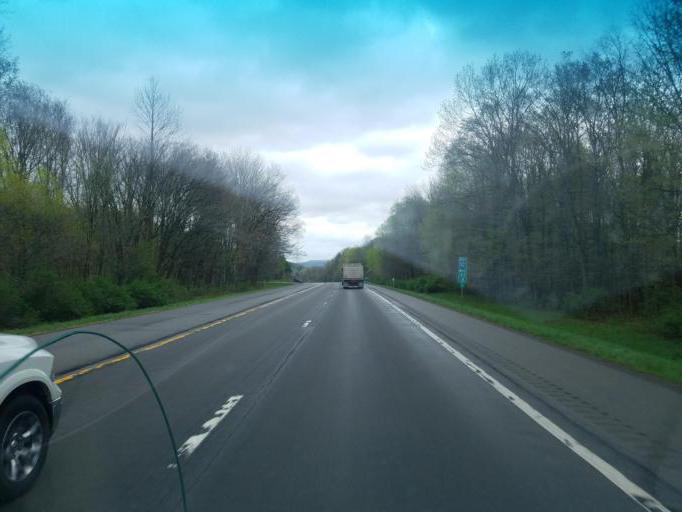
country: US
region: New York
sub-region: Chautauqua County
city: Falconer
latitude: 42.1344
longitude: -79.1359
